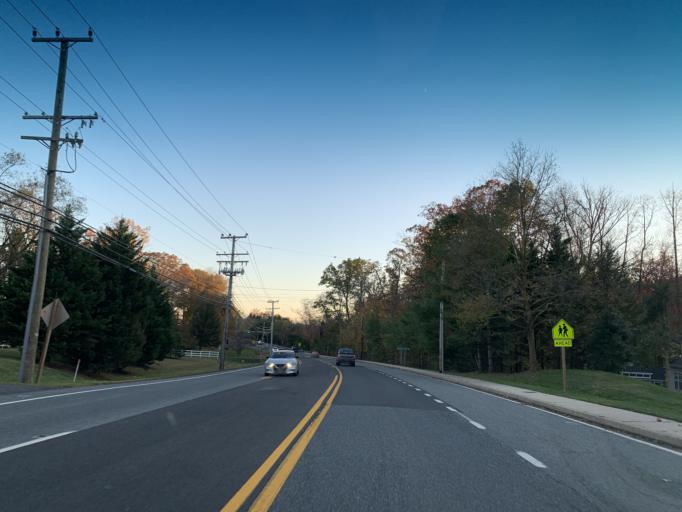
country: US
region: Maryland
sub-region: Harford County
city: South Bel Air
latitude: 39.5640
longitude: -76.3332
